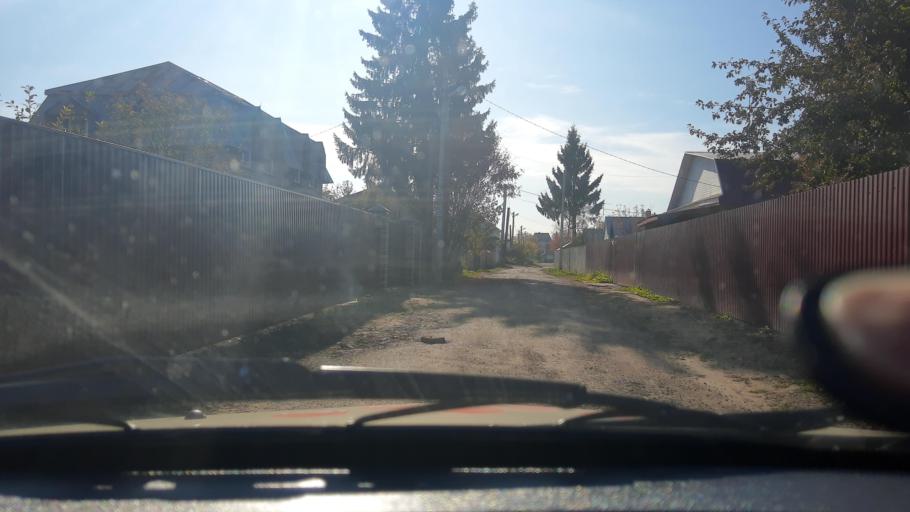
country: RU
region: Bashkortostan
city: Ufa
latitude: 54.8009
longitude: 56.1454
